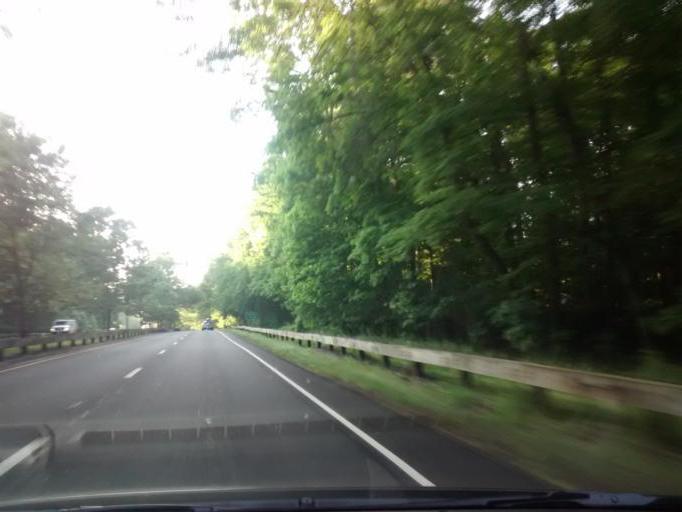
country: US
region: Connecticut
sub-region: Fairfield County
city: Cos Cob
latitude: 41.0910
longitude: -73.6278
